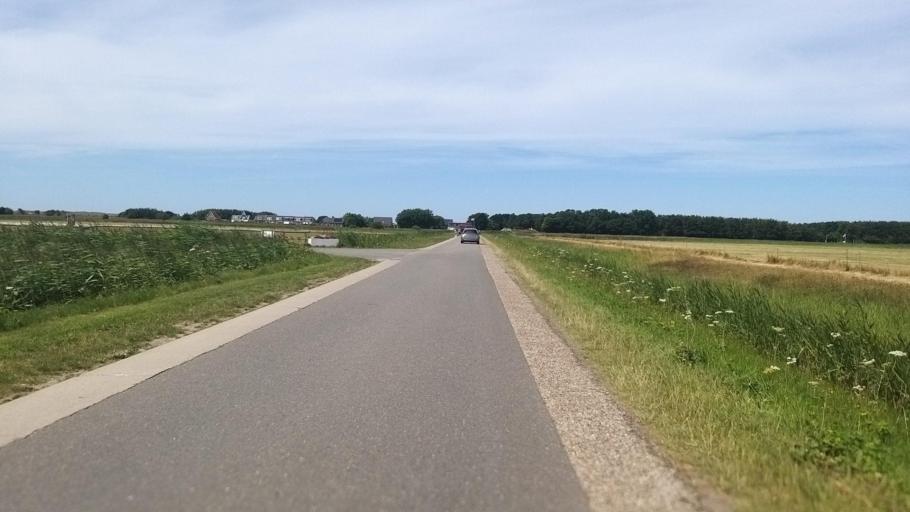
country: NL
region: North Holland
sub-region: Gemeente Texel
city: Den Burg
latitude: 53.1448
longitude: 4.8663
